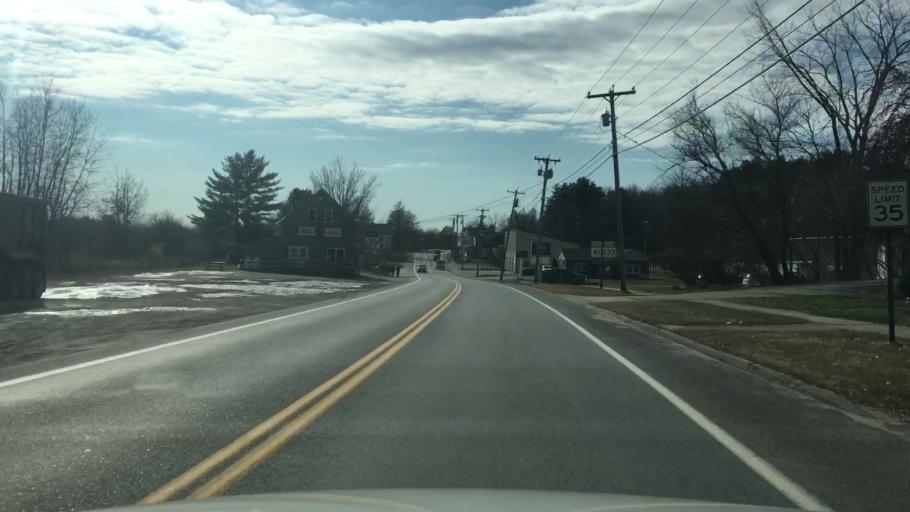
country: US
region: Maine
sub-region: Kennebec County
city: Winthrop
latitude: 44.3045
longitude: -69.9777
